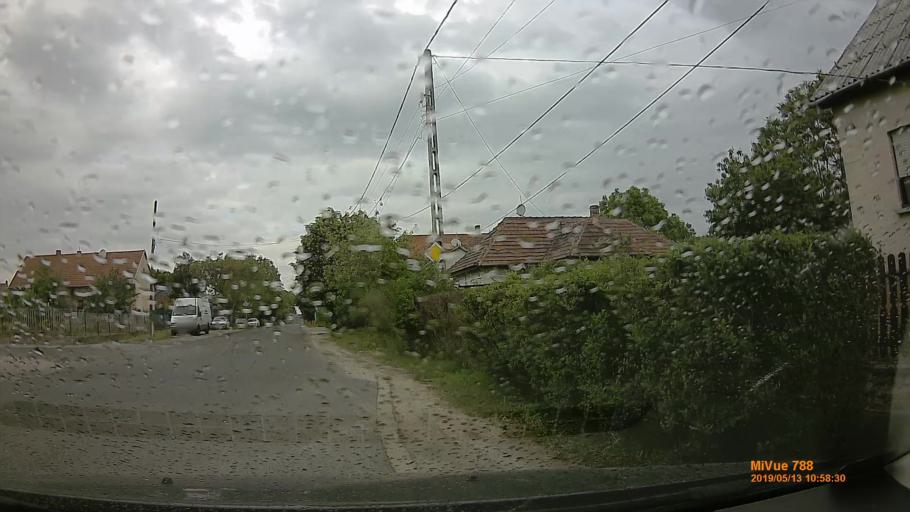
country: HU
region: Budapest
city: Budapest XXIII. keruelet
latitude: 47.3902
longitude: 19.0967
